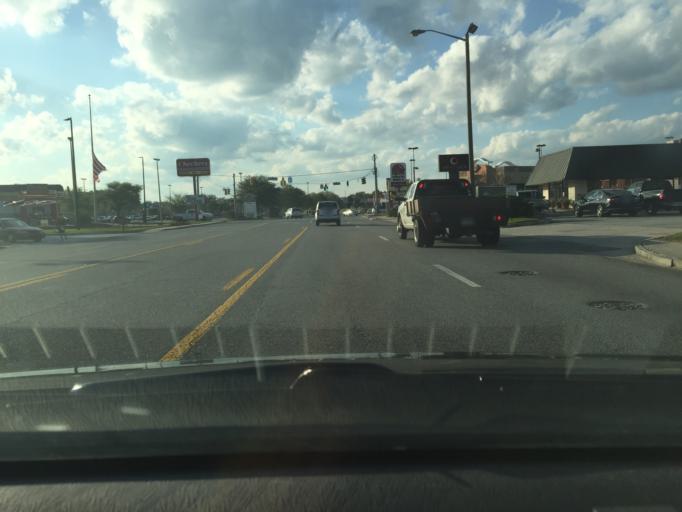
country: US
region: Georgia
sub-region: Chatham County
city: Isle of Hope
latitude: 32.0038
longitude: -81.1132
